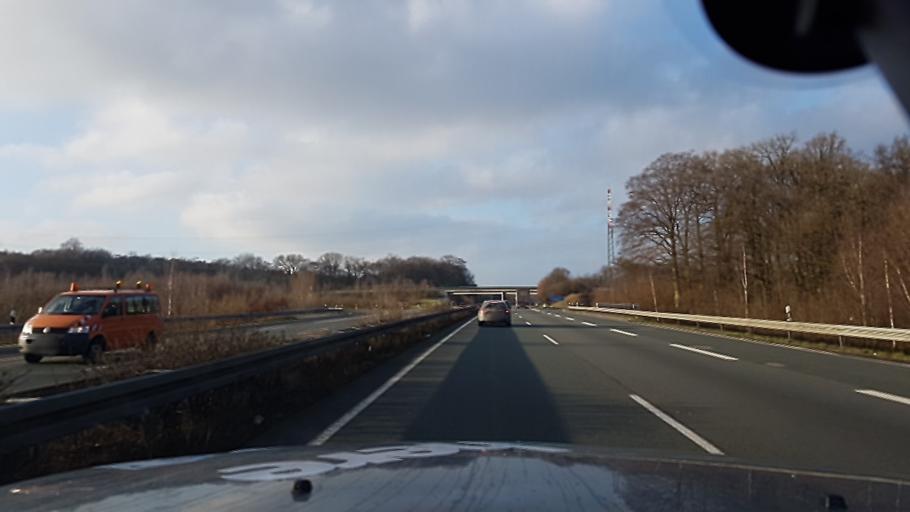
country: DE
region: North Rhine-Westphalia
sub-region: Regierungsbezirk Munster
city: Birgte
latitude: 52.2694
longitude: 7.6611
